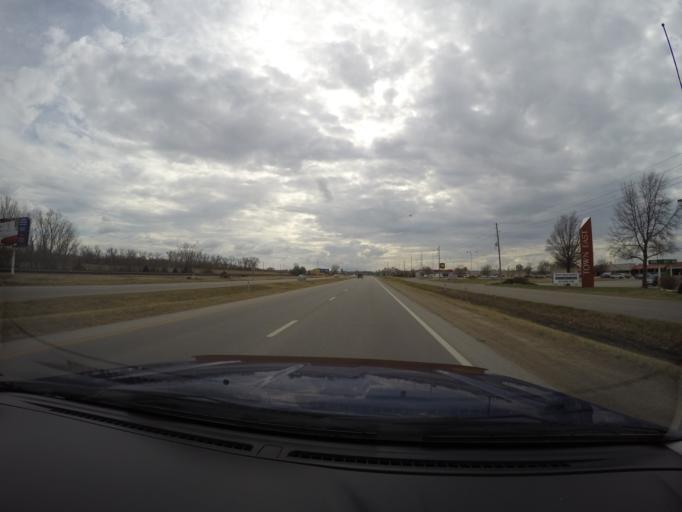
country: US
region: Kansas
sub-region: Riley County
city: Manhattan
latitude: 39.1850
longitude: -96.5501
